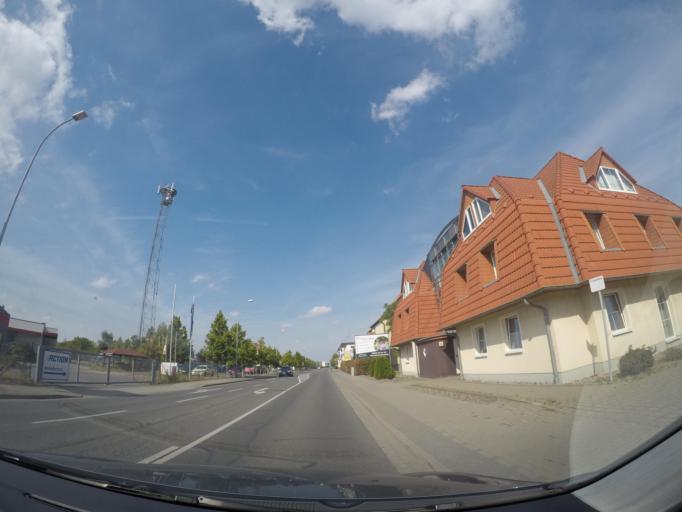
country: DE
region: Saxony-Anhalt
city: Wernigerode
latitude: 51.8432
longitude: 10.7823
